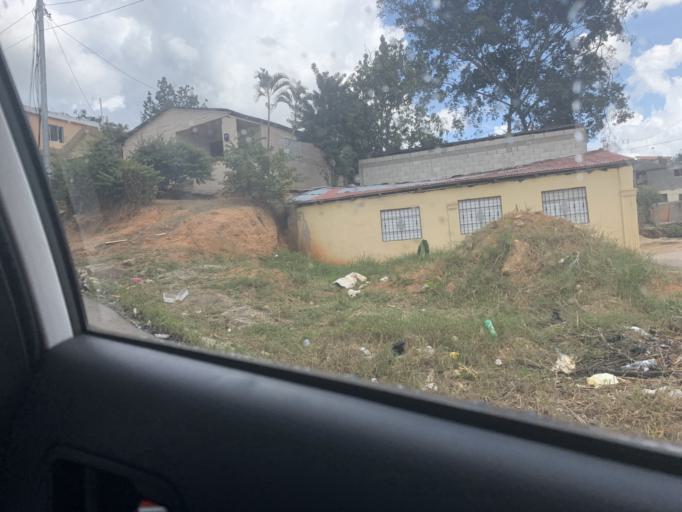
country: DO
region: Monte Plata
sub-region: Yamasa
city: Yamasa
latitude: 18.7706
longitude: -70.0223
